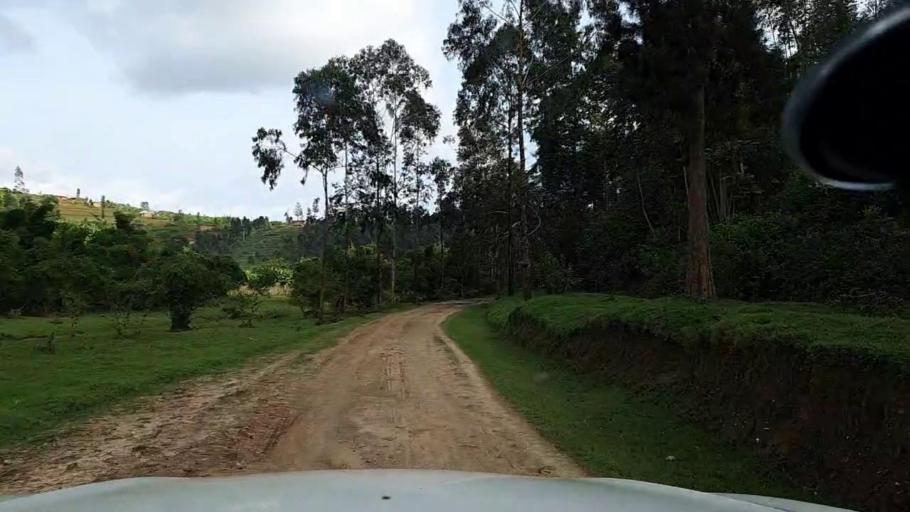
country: RW
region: Western Province
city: Kibuye
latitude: -2.1551
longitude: 29.5443
